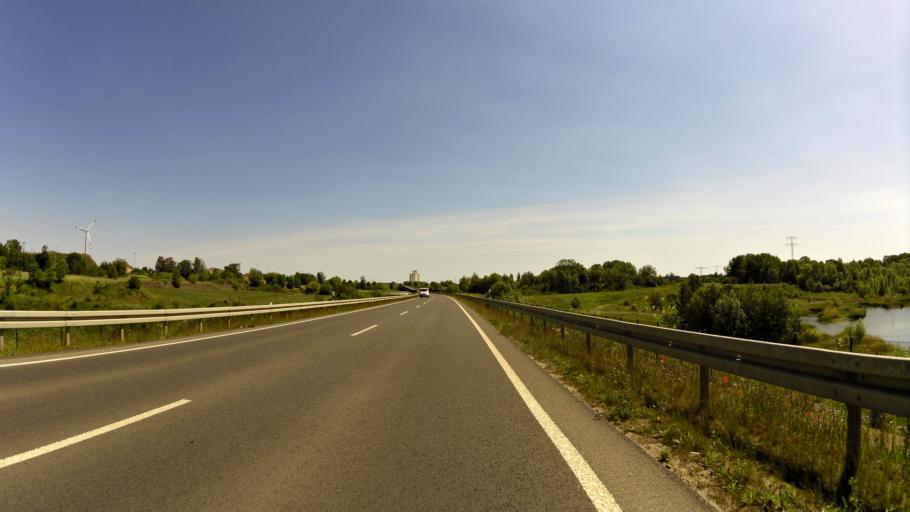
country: DE
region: Brandenburg
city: Rehfelde
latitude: 52.4885
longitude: 13.8521
